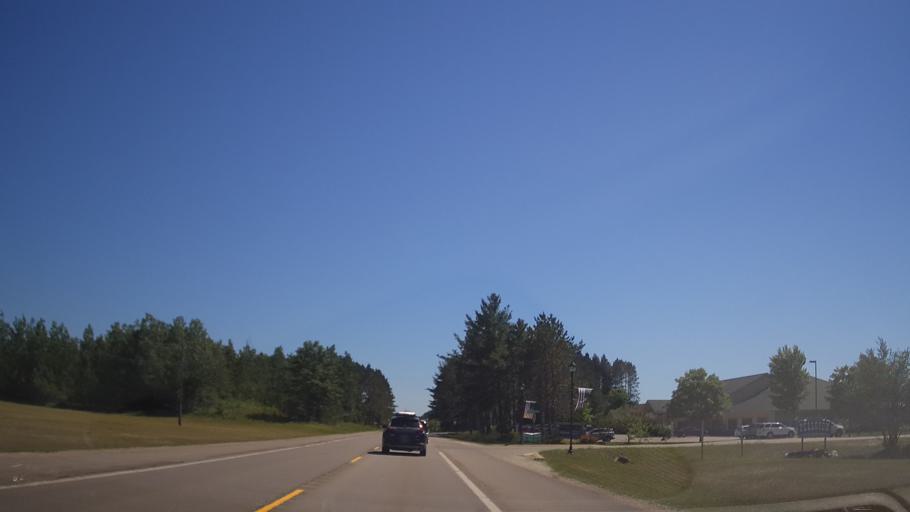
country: US
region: Michigan
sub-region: Cheboygan County
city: Indian River
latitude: 45.5586
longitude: -84.7842
